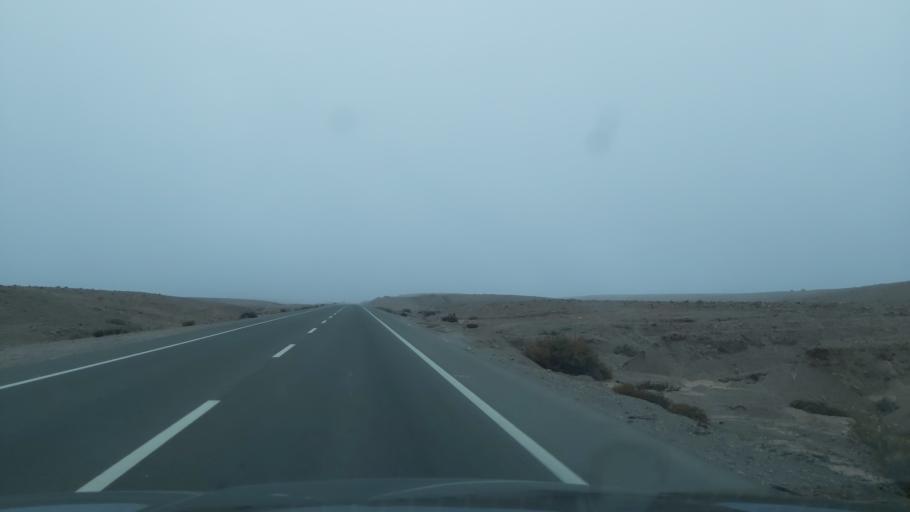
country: CL
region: Atacama
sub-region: Provincia de Copiapo
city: Copiapo
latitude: -27.2848
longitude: -70.0989
